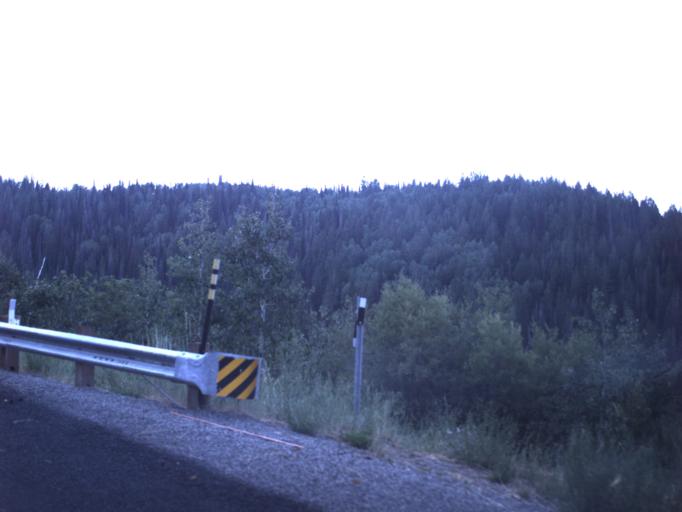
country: US
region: Utah
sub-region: Summit County
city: Francis
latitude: 40.5081
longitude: -111.0463
